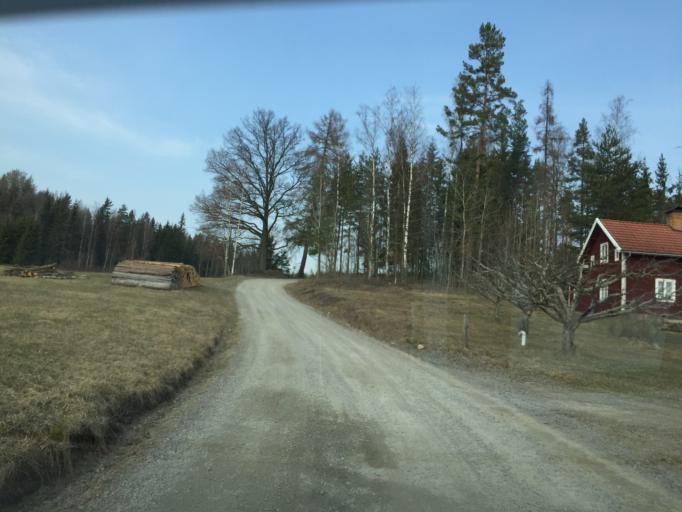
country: SE
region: Soedermanland
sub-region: Vingakers Kommun
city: Vingaker
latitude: 59.0250
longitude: 15.7778
